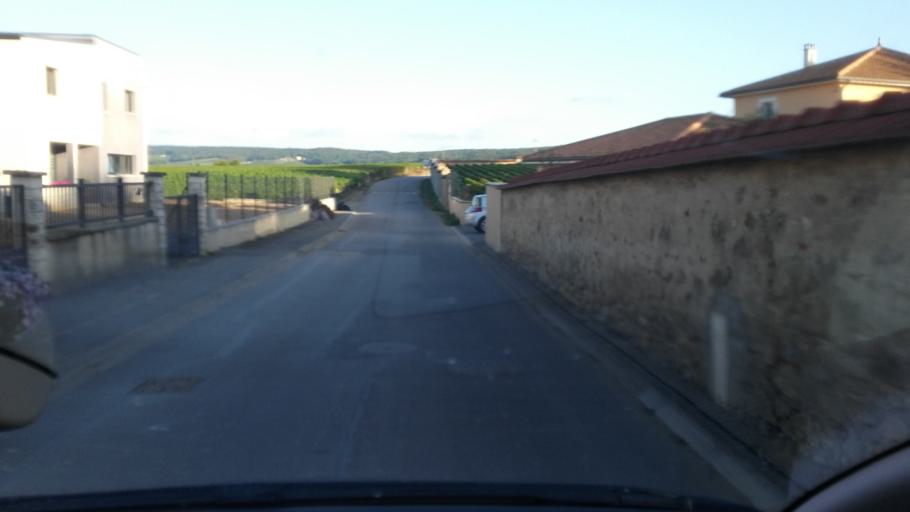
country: FR
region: Champagne-Ardenne
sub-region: Departement de la Marne
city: Rilly-la-Montagne
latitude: 49.1667
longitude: 4.0486
